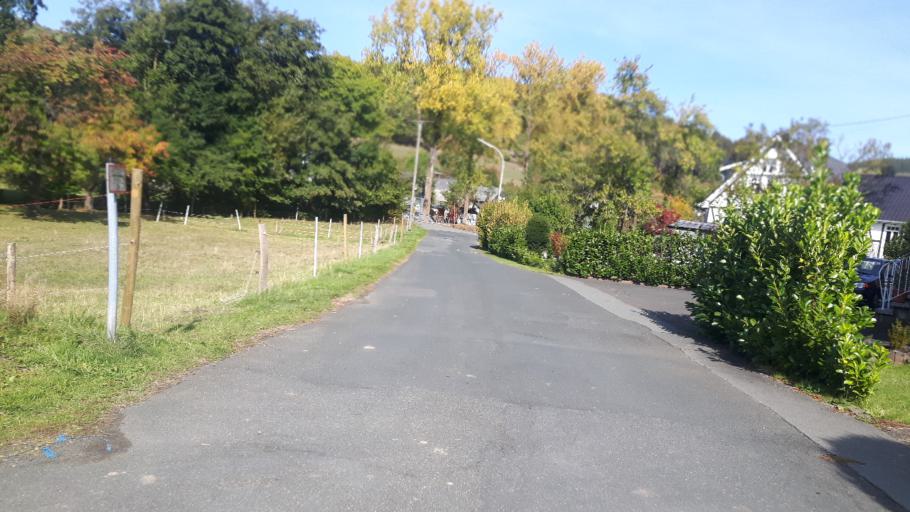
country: DE
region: North Rhine-Westphalia
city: Netphen
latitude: 50.8923
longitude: 8.1902
